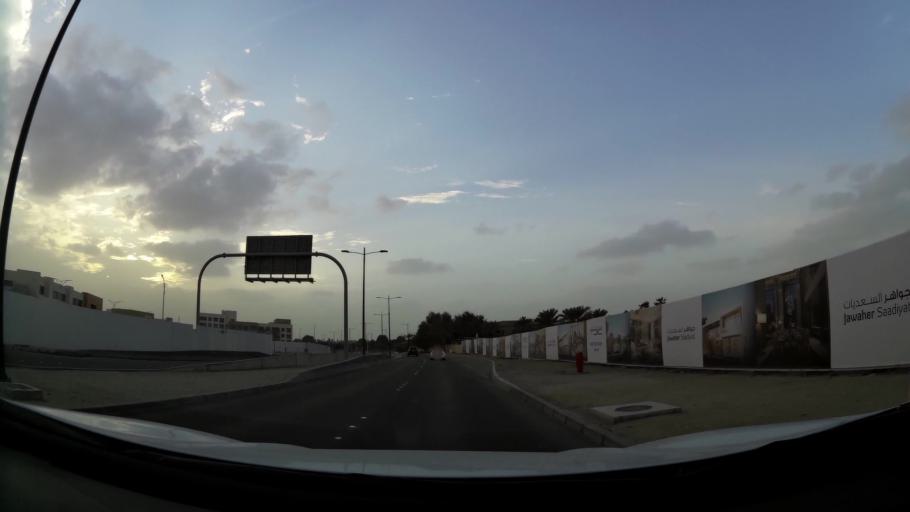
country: AE
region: Abu Dhabi
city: Abu Dhabi
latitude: 24.5332
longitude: 54.4240
